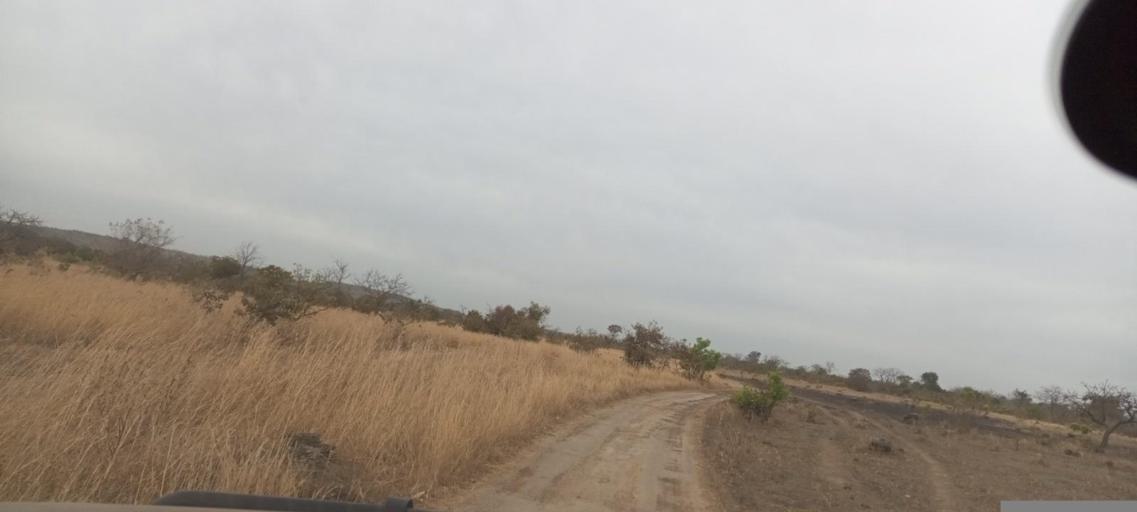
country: ML
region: Koulikoro
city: Kati
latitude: 12.7707
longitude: -8.3817
